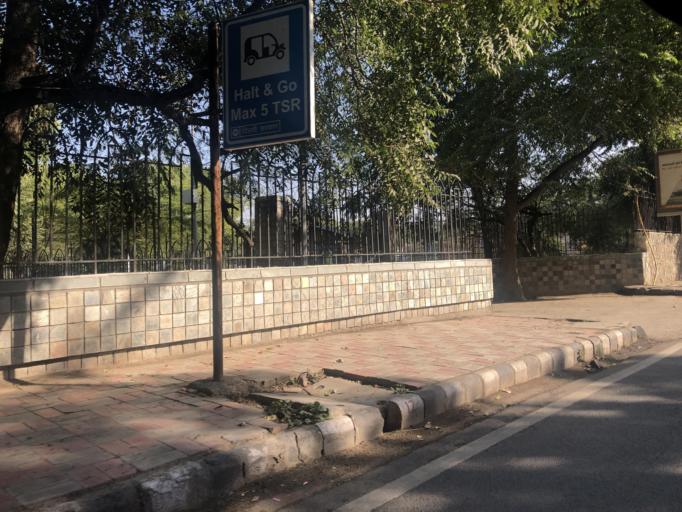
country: IN
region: NCT
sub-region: Central Delhi
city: Karol Bagh
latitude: 28.5547
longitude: 77.1647
